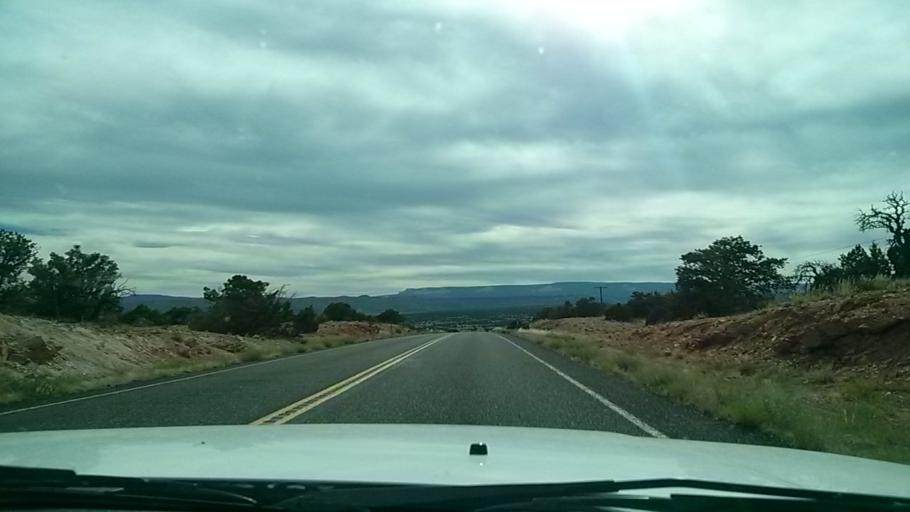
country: US
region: Utah
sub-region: Wayne County
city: Loa
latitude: 37.7506
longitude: -111.4679
